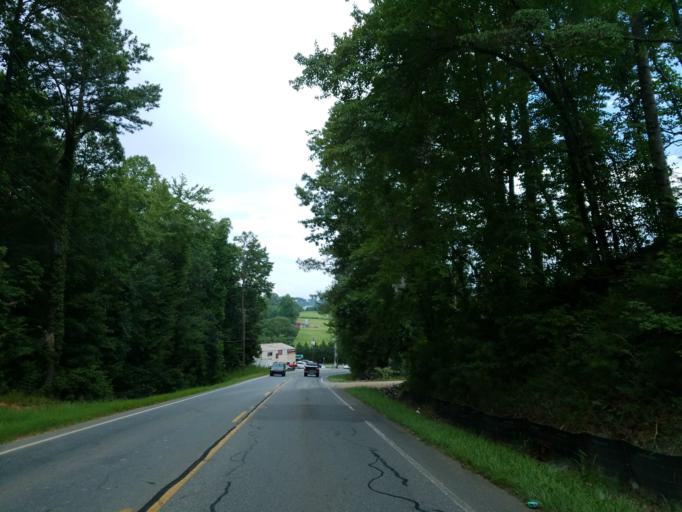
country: US
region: Georgia
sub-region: Gilmer County
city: Ellijay
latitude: 34.6412
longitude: -84.5101
